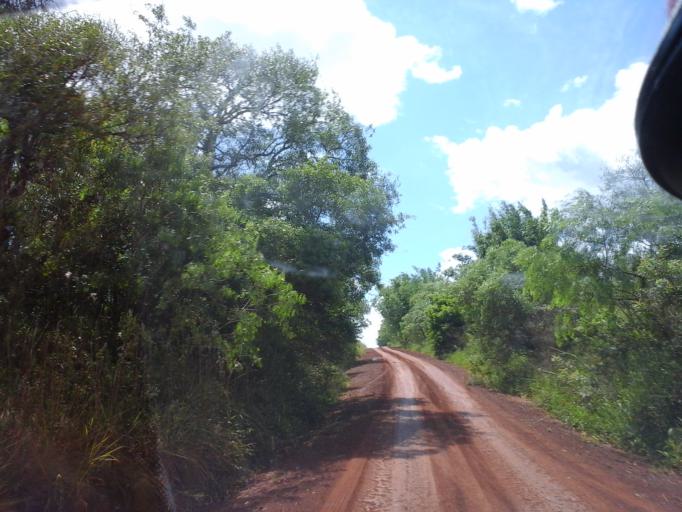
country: AR
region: Misiones
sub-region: Departamento de Apostoles
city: Apostoles
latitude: -27.9746
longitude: -55.7743
